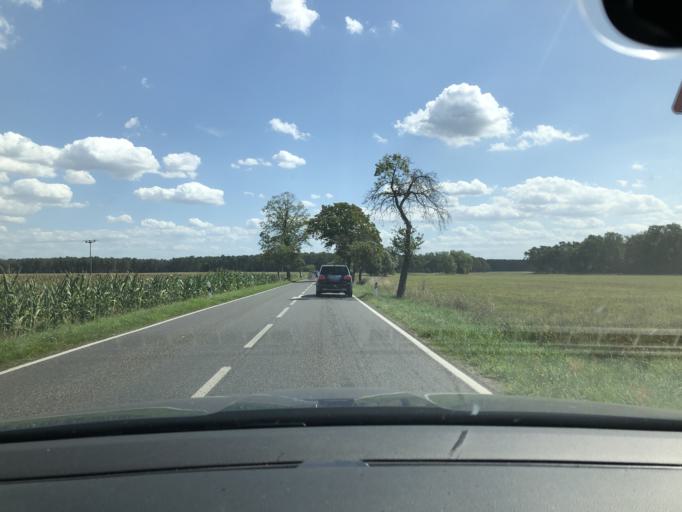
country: DE
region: Brandenburg
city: Ruthnick
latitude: 52.8973
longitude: 12.9747
